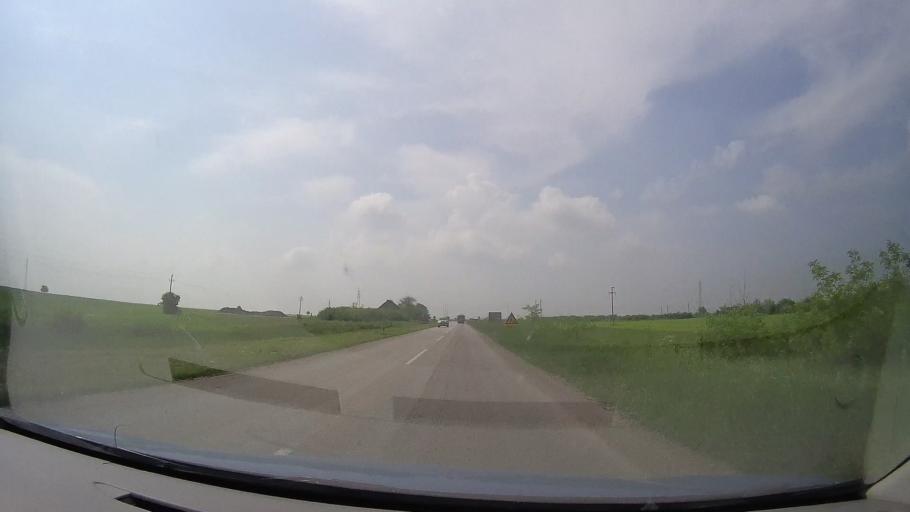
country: RS
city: Debeljaca
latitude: 45.0729
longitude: 20.6407
